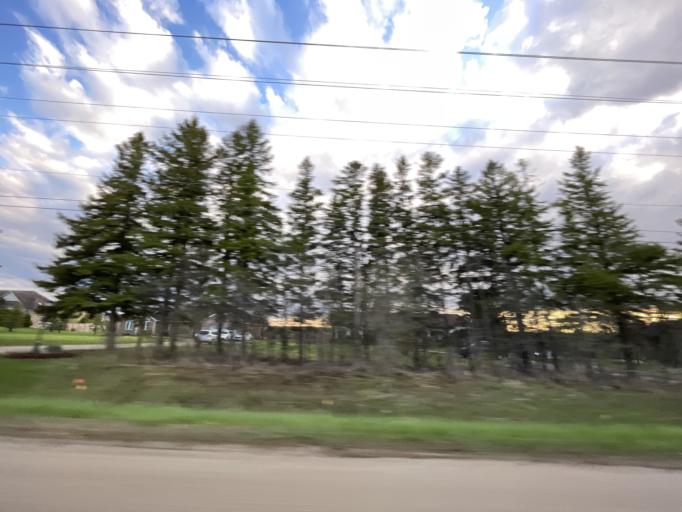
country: CA
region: Ontario
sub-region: Wellington County
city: Guelph
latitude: 43.5948
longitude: -80.2835
